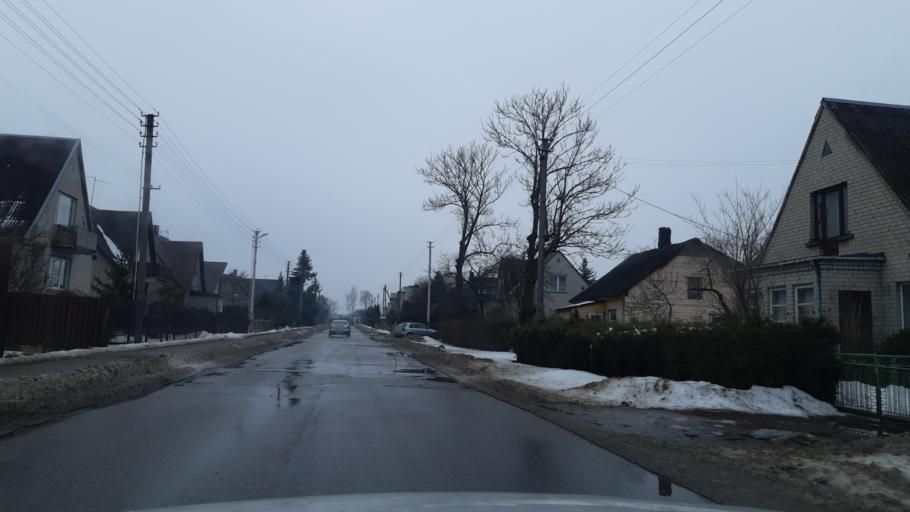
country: LT
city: Vilkaviskis
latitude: 54.6474
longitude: 23.0210
